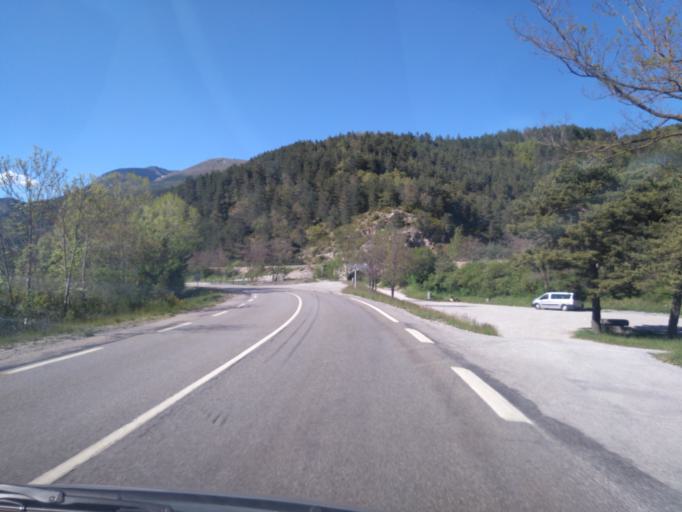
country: FR
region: Provence-Alpes-Cote d'Azur
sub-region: Departement des Hautes-Alpes
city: Veynes
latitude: 44.5549
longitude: 5.7672
